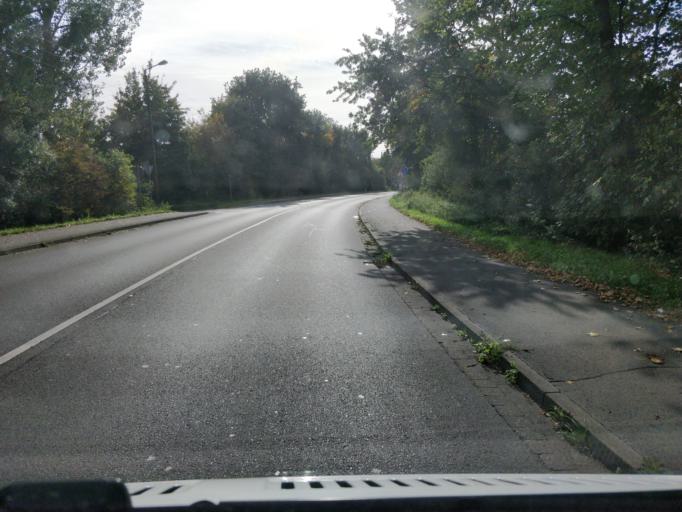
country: DE
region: North Rhine-Westphalia
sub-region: Regierungsbezirk Dusseldorf
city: Dinslaken
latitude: 51.5493
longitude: 6.7331
